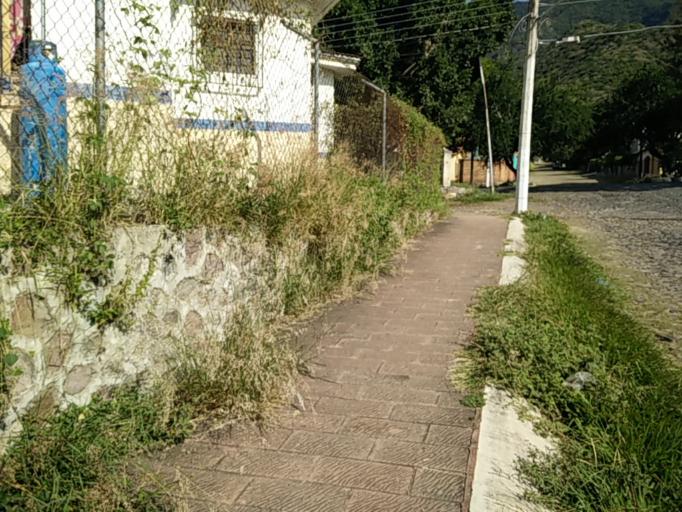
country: MX
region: Jalisco
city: Ajijic
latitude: 20.3006
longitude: -103.2761
